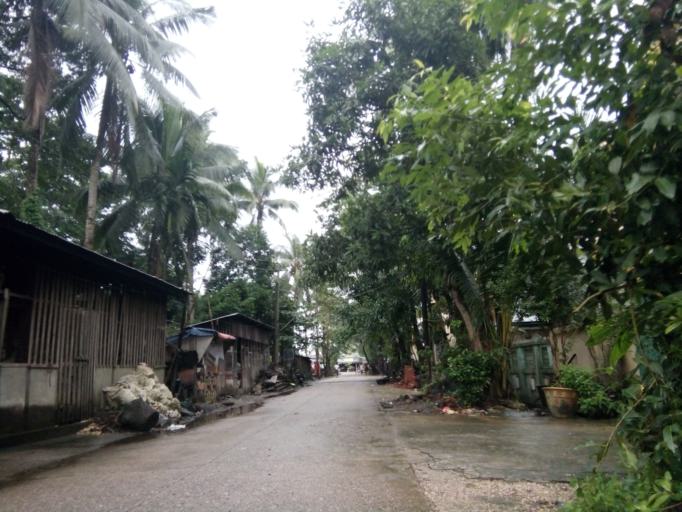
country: MM
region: Yangon
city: Yangon
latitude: 16.9190
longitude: 96.1597
